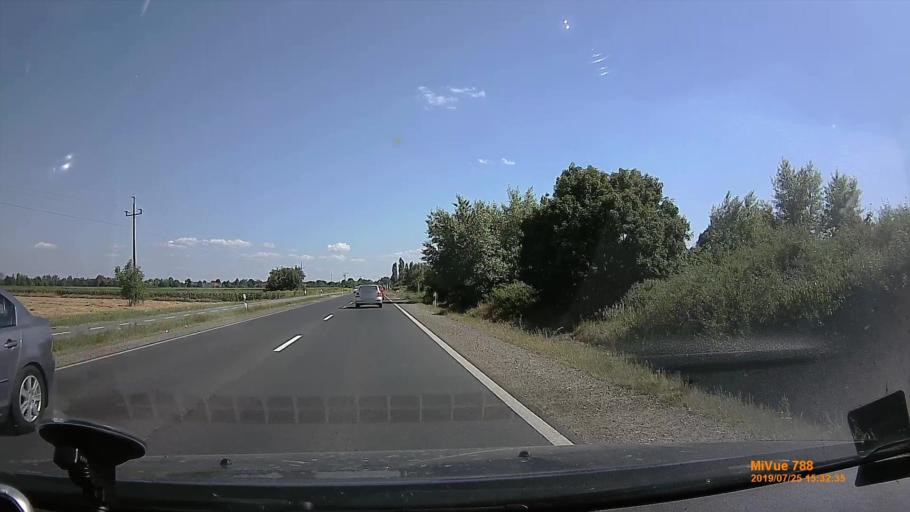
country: HU
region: Borsod-Abauj-Zemplen
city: Malyi
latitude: 48.0049
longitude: 20.8293
